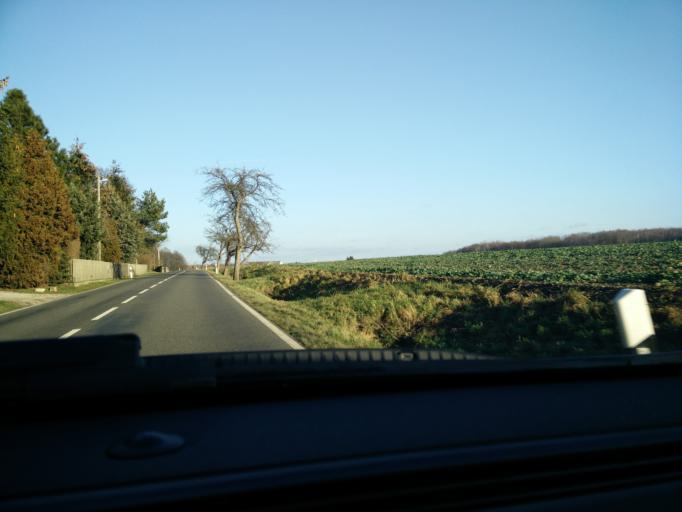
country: DE
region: Saxony
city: Geithain
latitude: 51.0673
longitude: 12.7133
